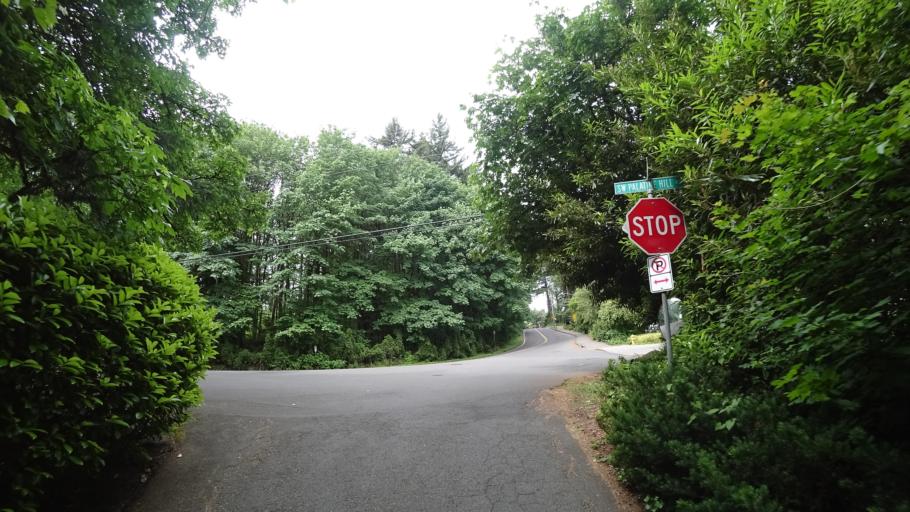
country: US
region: Oregon
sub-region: Clackamas County
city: Lake Oswego
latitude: 45.4468
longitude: -122.6695
